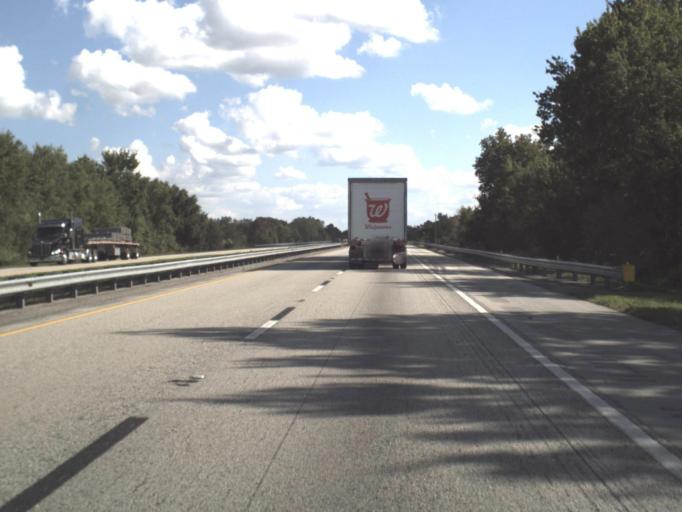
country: US
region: Florida
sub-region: Indian River County
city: Fellsmere
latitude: 27.7460
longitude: -80.9332
